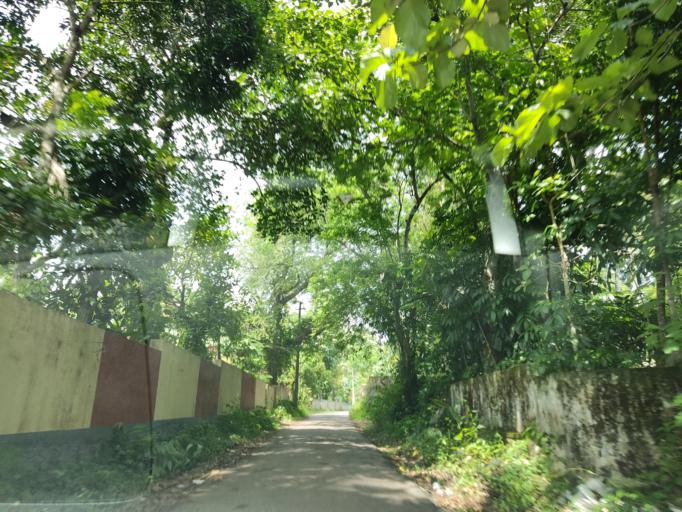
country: IN
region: Kerala
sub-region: Alappuzha
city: Mavelikara
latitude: 9.2581
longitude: 76.5649
